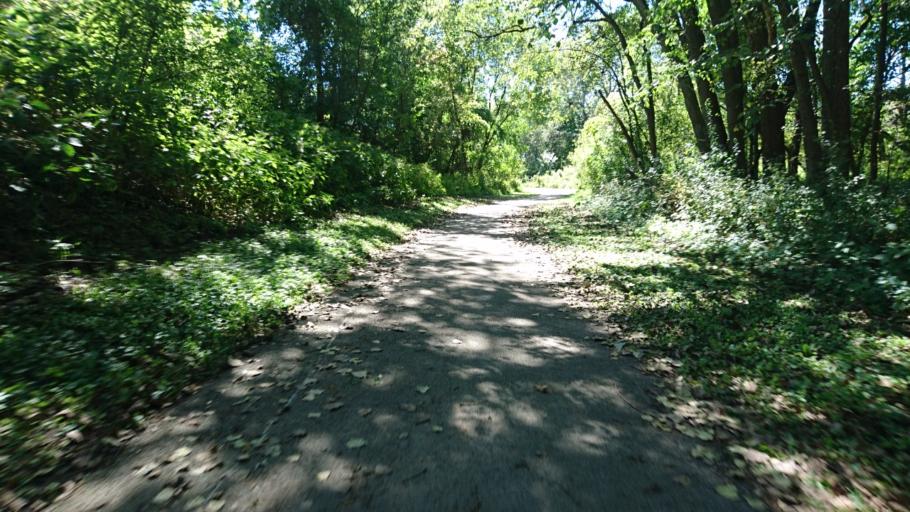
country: US
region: Illinois
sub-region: Cook County
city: Chicago Heights
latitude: 41.5220
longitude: -87.6235
